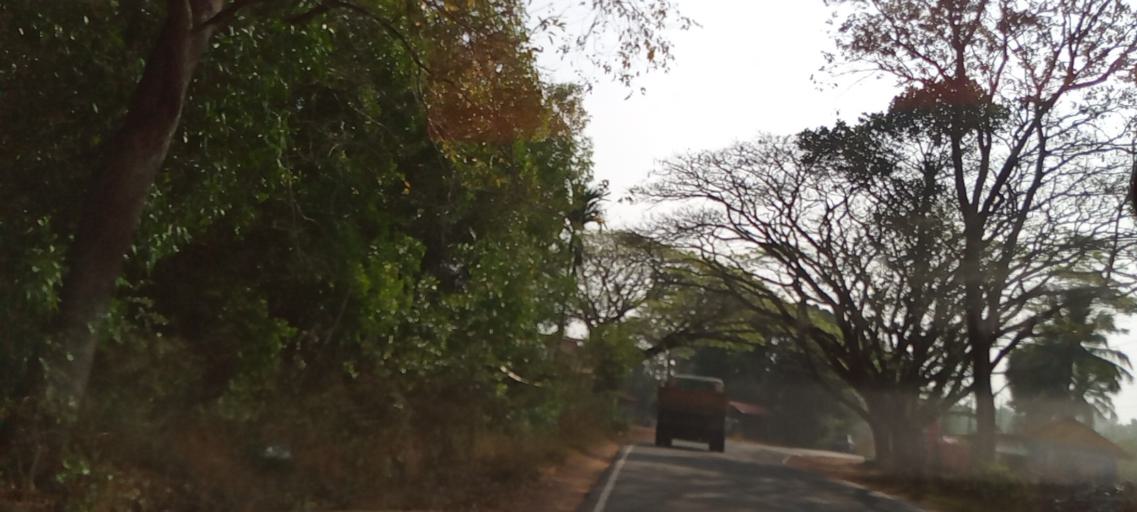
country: IN
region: Karnataka
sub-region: Udupi
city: Coondapoor
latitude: 13.5174
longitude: 74.7623
